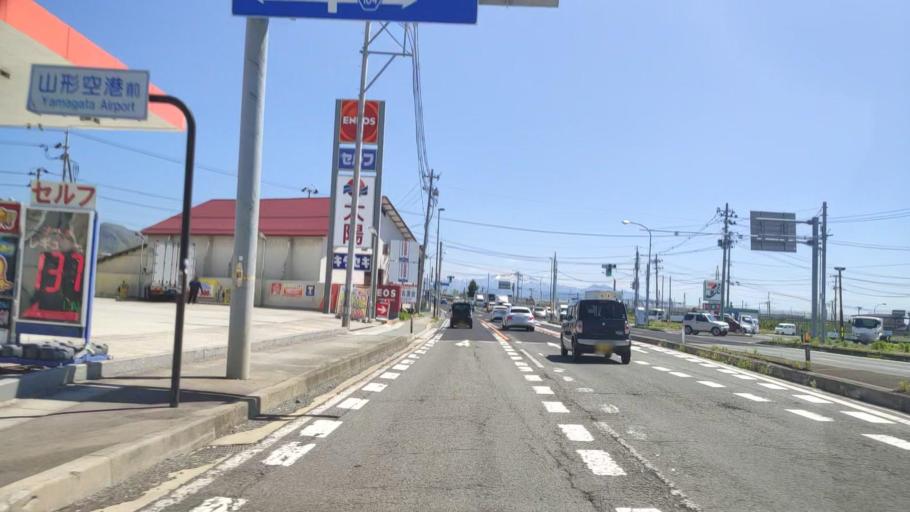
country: JP
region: Yamagata
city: Higashine
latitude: 38.4013
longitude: 140.3740
